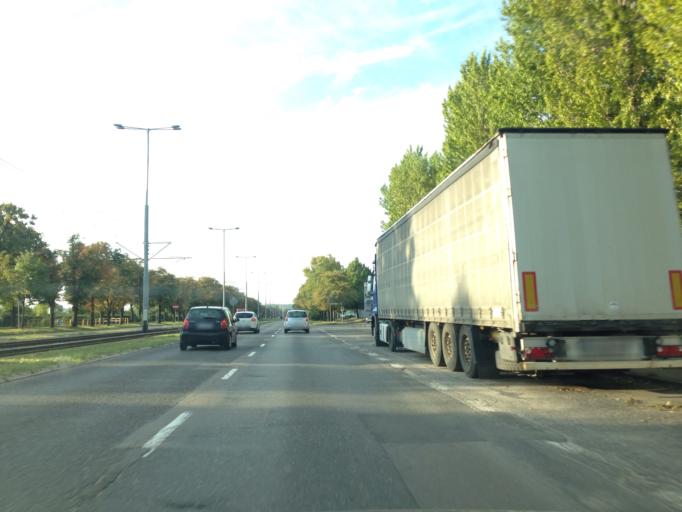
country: PL
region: Pomeranian Voivodeship
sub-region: Gdansk
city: Gdansk
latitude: 54.3956
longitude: 18.6221
